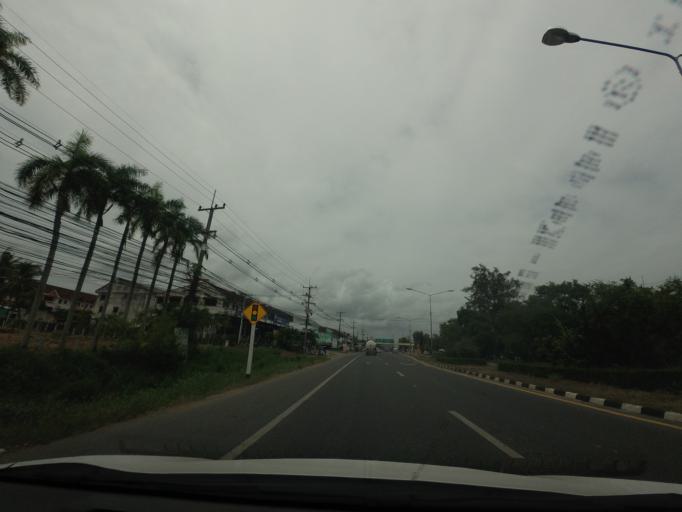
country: TH
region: Chon Buri
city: Sattahip
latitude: 12.6874
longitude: 100.9745
